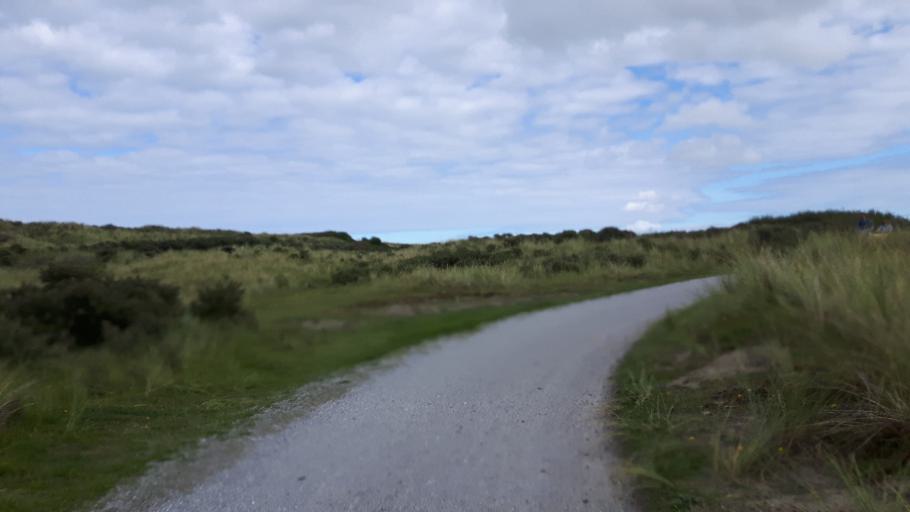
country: NL
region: Friesland
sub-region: Gemeente Ameland
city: Nes
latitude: 53.4572
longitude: 5.7364
